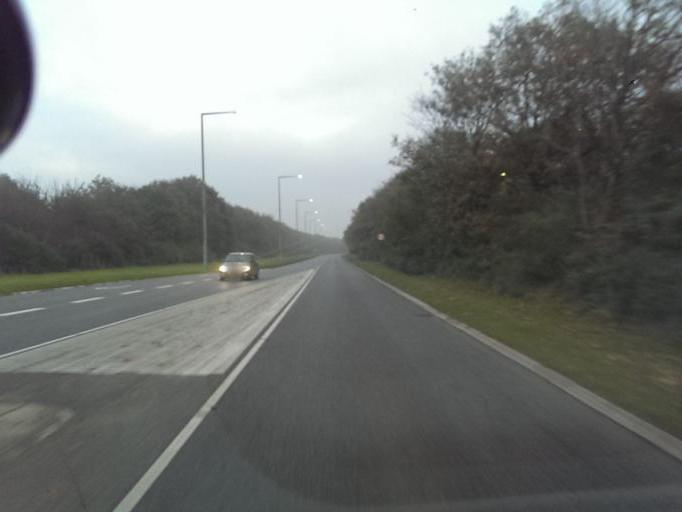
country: DK
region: South Denmark
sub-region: Esbjerg Kommune
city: Esbjerg
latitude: 55.5064
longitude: 8.4328
